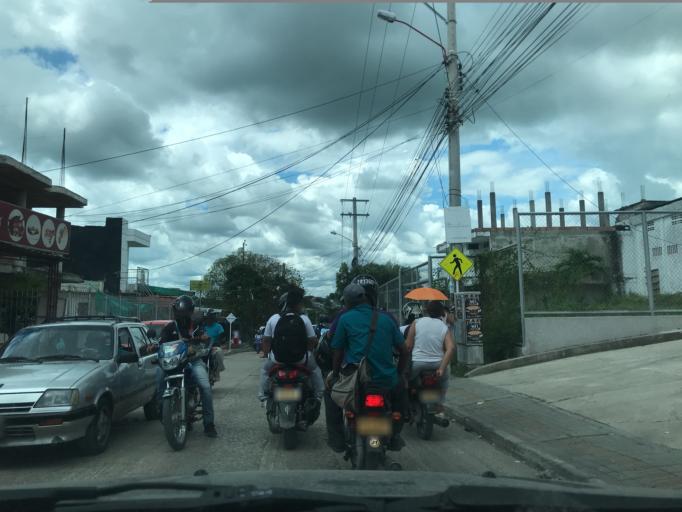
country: CO
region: Sucre
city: Sincelejo
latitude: 9.3100
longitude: -75.3984
